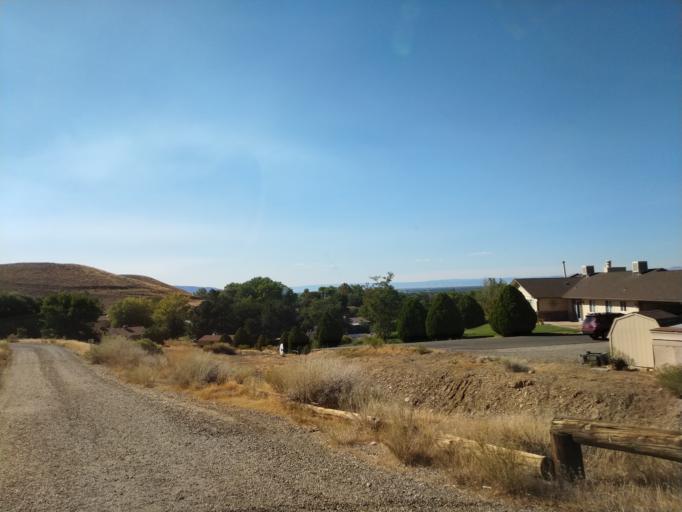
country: US
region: Colorado
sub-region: Mesa County
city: Orchard Mesa
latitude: 39.0245
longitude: -108.5137
